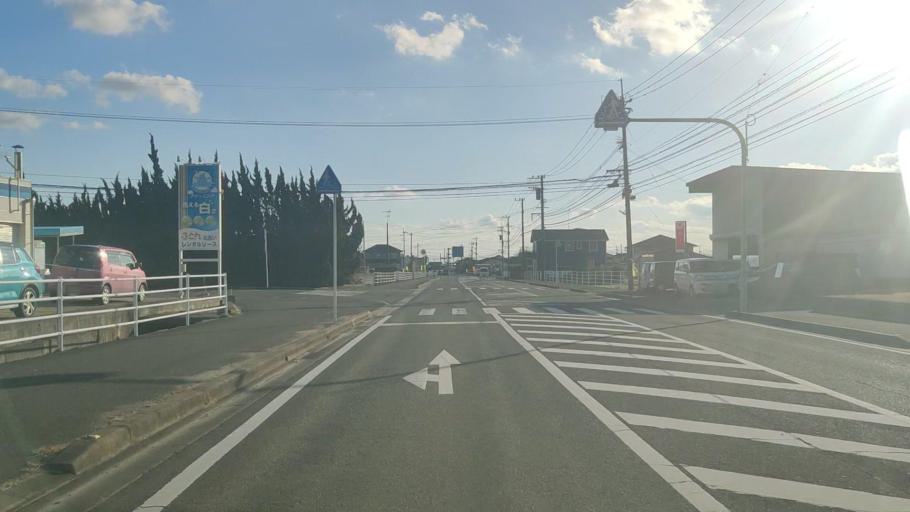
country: JP
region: Saga Prefecture
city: Saga-shi
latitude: 33.3118
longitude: 130.2650
